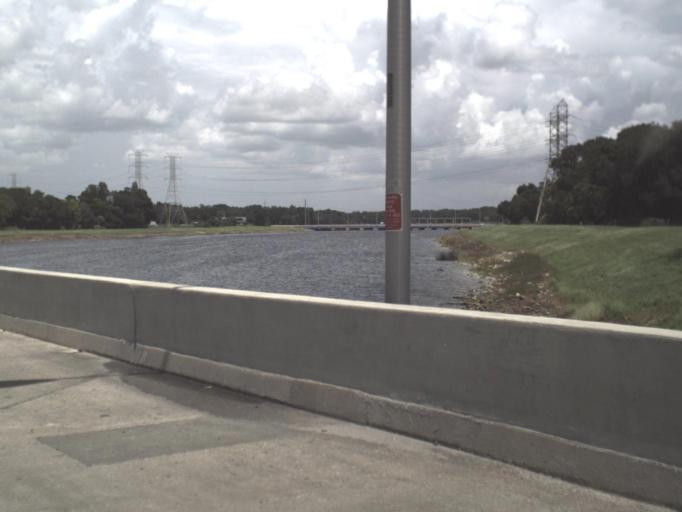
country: US
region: Florida
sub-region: Hillsborough County
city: East Lake-Orient Park
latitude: 27.9756
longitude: -82.3603
